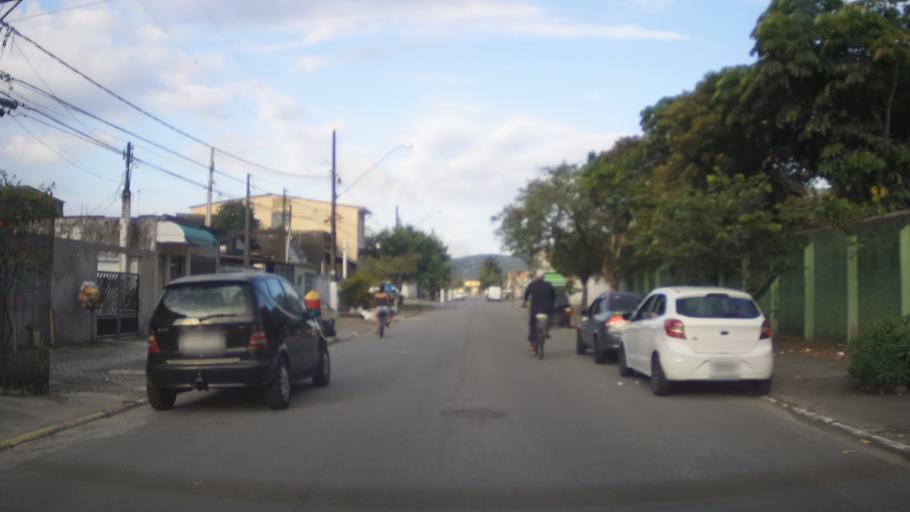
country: BR
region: Sao Paulo
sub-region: Praia Grande
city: Praia Grande
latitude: -23.9955
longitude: -46.4230
